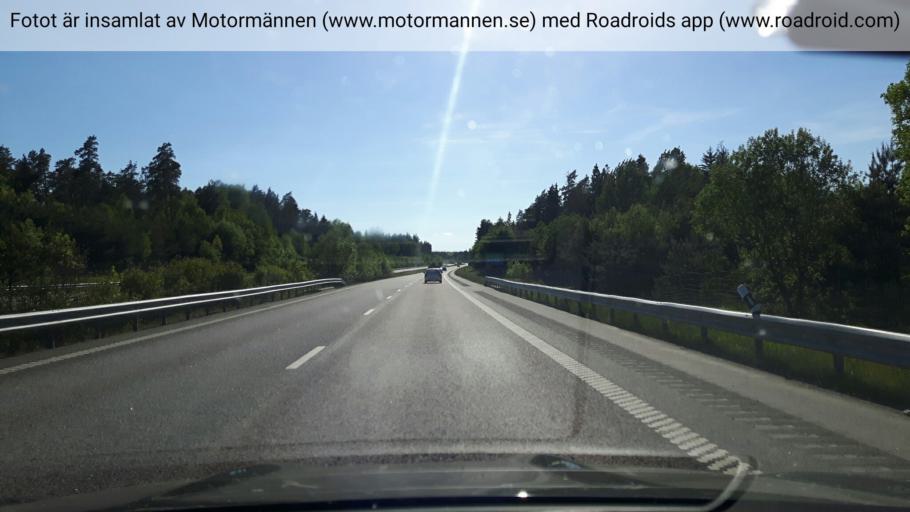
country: SE
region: Stockholm
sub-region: Norrtalje Kommun
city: Rimbo
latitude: 59.7083
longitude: 18.5211
